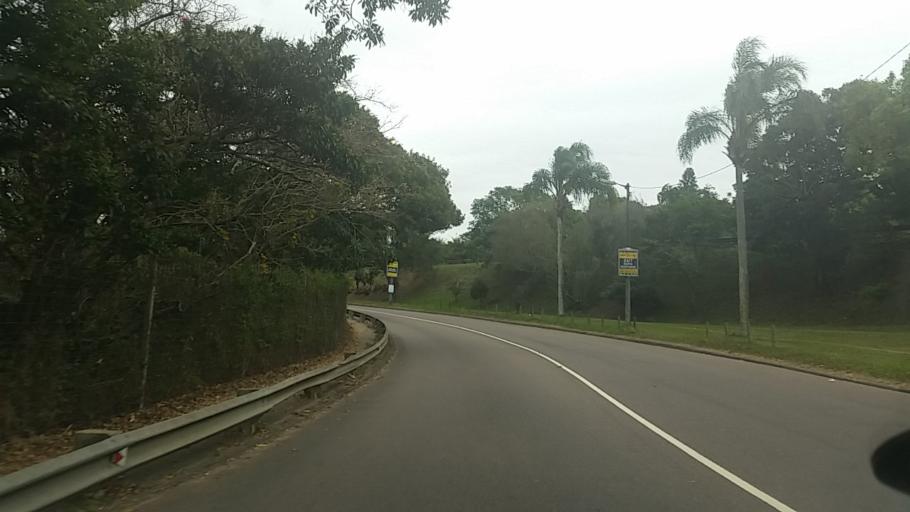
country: ZA
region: KwaZulu-Natal
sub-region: eThekwini Metropolitan Municipality
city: Berea
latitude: -29.8339
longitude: 30.9221
